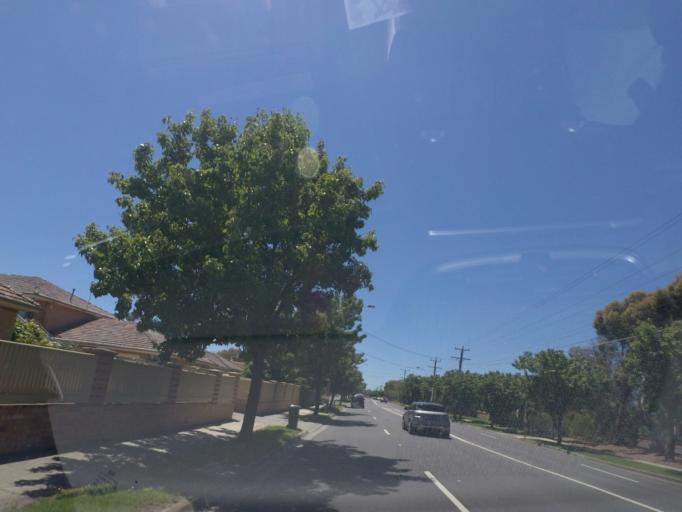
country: AU
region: Victoria
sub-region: Whittlesea
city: Lalor
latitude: -37.6694
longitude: 145.0158
